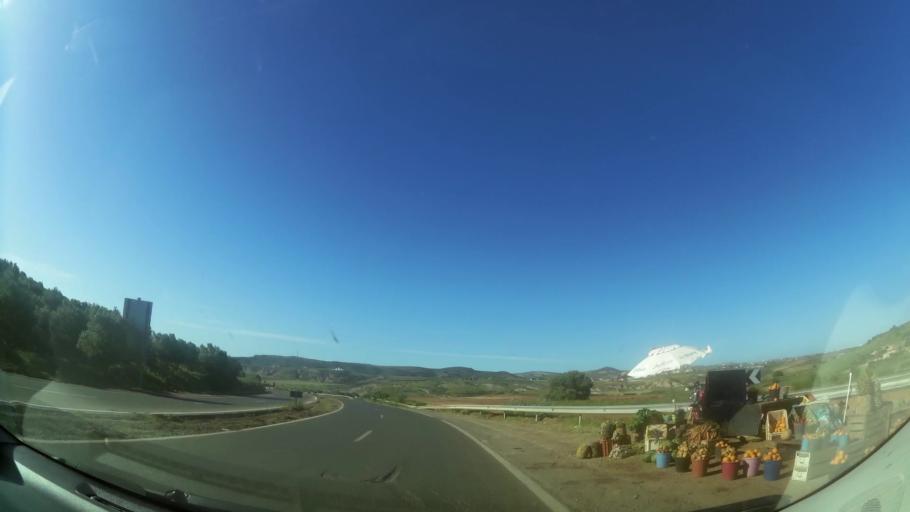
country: MA
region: Oriental
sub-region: Berkane-Taourirt
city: Ahfir
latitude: 35.0319
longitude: -2.2030
